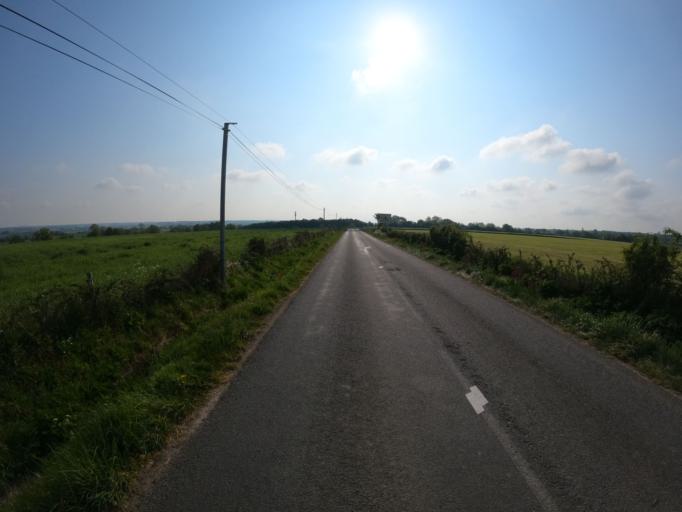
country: FR
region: Pays de la Loire
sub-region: Departement de Maine-et-Loire
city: La Romagne
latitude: 47.0646
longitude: -1.0352
